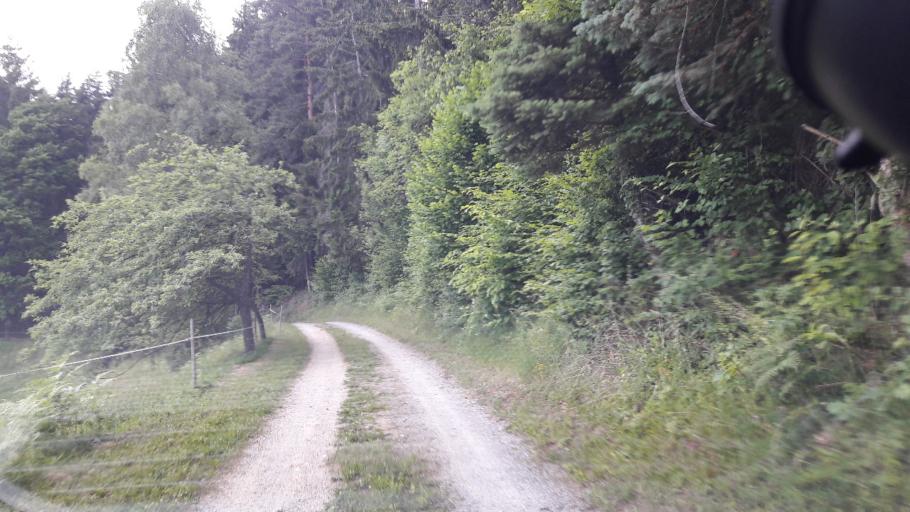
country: AT
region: Styria
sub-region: Politischer Bezirk Graz-Umgebung
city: Stiwoll
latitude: 47.1242
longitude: 15.2236
